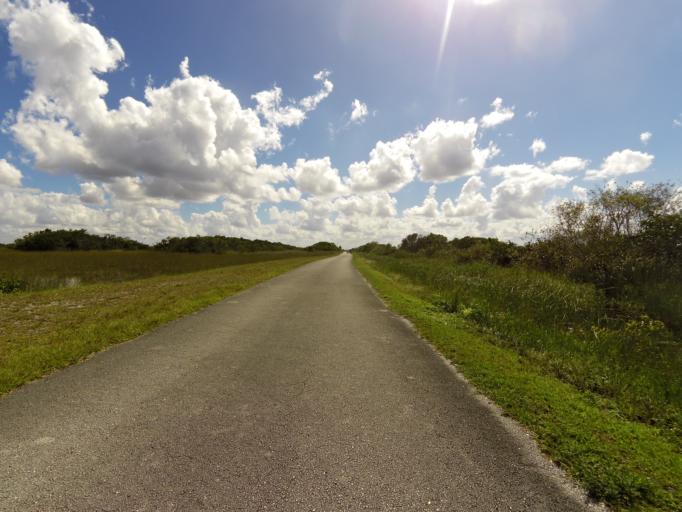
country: US
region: Florida
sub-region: Miami-Dade County
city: The Hammocks
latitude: 25.7060
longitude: -80.7668
